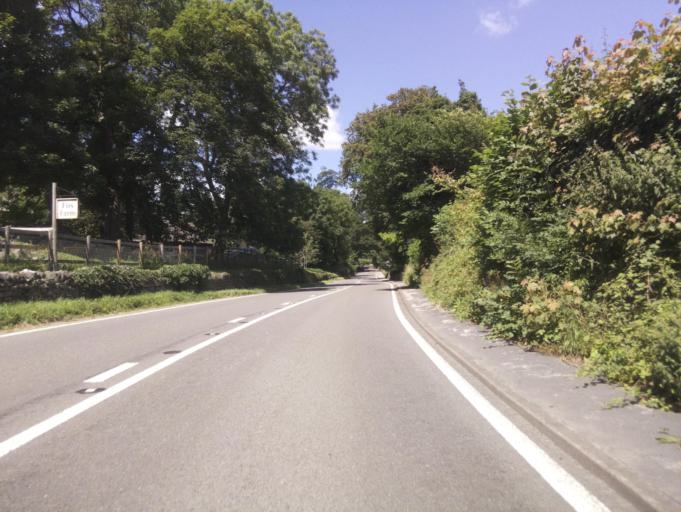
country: GB
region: England
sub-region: Derbyshire
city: Ashbourne
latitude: 53.0495
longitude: -1.7407
